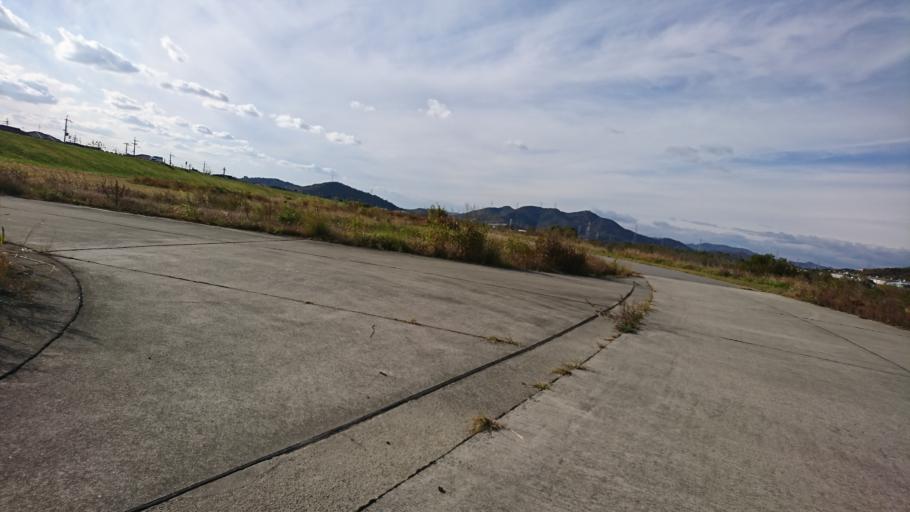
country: JP
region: Hyogo
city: Kakogawacho-honmachi
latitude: 34.7934
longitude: 134.8865
